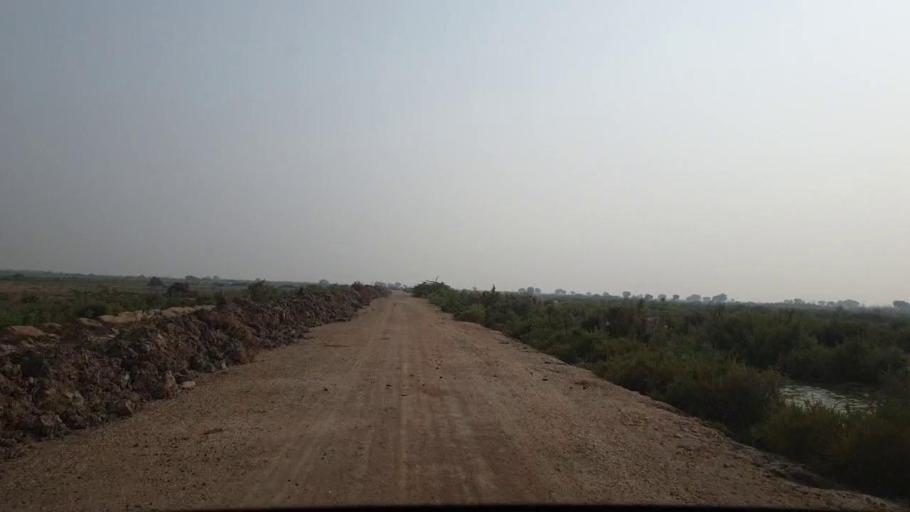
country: PK
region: Sindh
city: Jati
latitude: 24.2834
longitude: 68.4170
